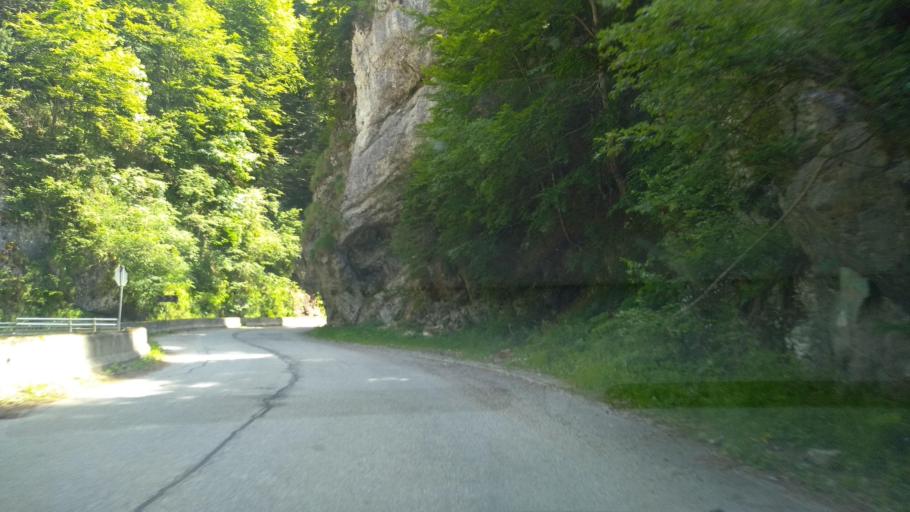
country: RO
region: Gorj
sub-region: Comuna Runcu
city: Valea Mare
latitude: 45.2733
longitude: 22.9582
